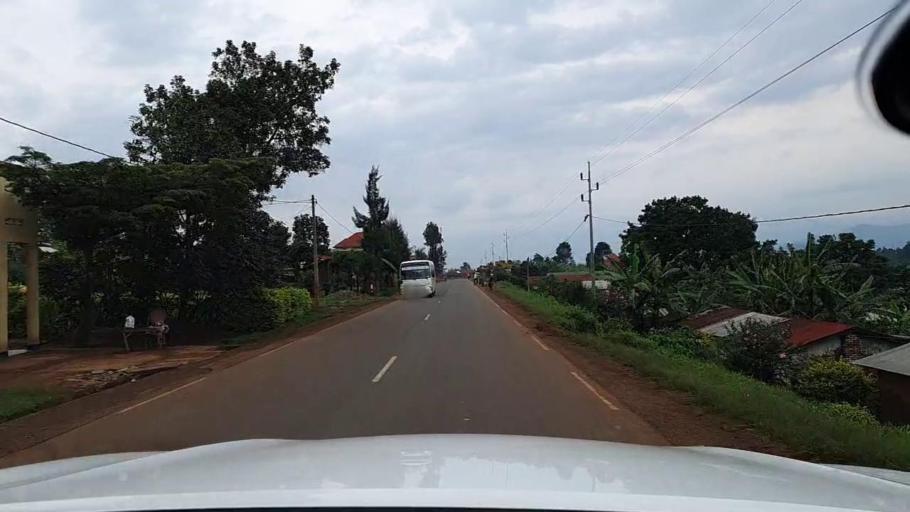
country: RW
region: Western Province
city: Cyangugu
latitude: -2.6416
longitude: 28.9531
